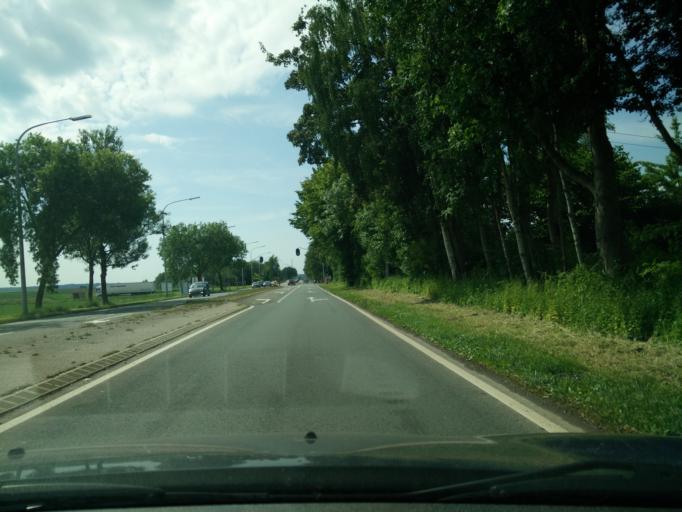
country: BE
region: Wallonia
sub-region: Province du Hainaut
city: Gerpinnes
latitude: 50.3119
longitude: 4.4794
